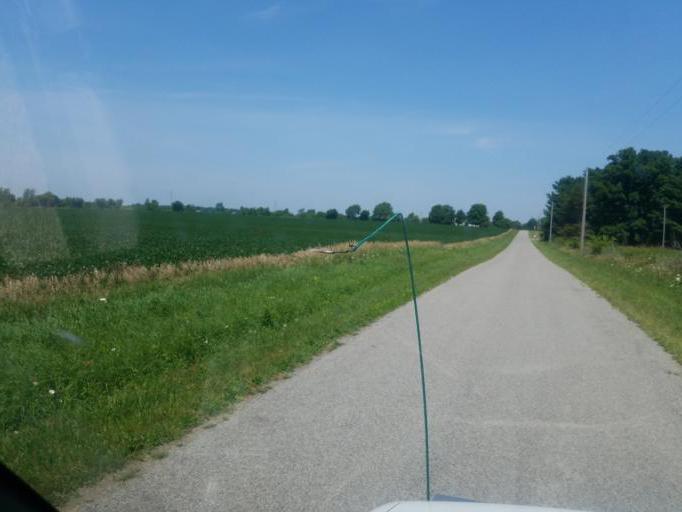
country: US
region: Ohio
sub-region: Logan County
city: West Liberty
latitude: 40.2818
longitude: -83.7684
